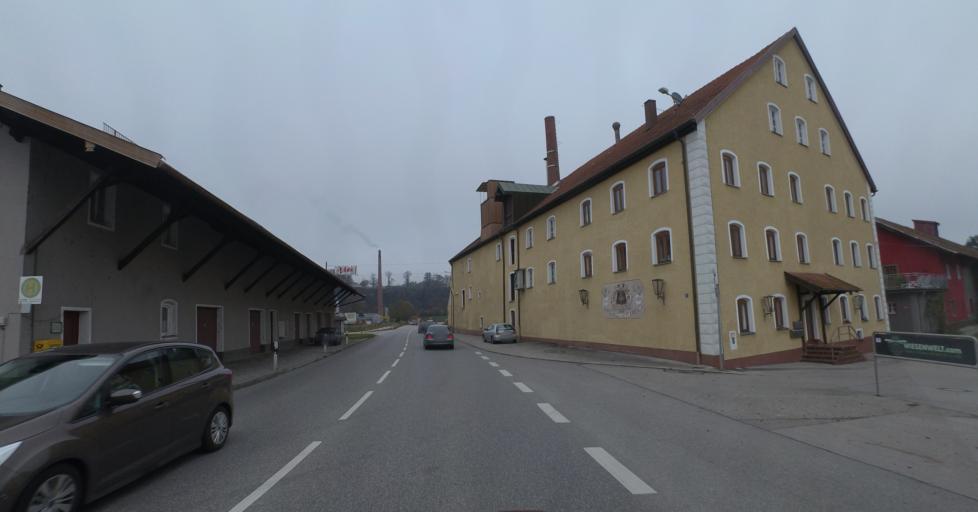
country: DE
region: Bavaria
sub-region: Upper Bavaria
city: Engelsberg
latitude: 48.1055
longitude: 12.5657
